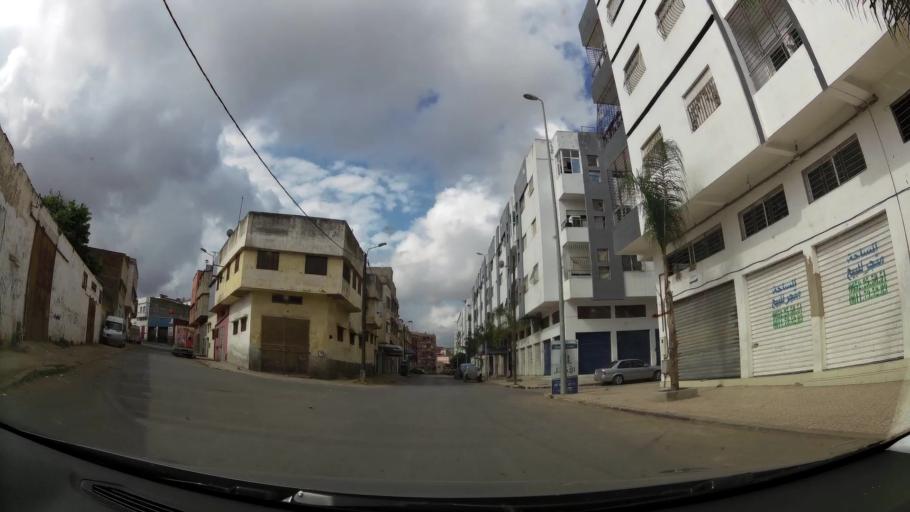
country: MA
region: Gharb-Chrarda-Beni Hssen
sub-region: Kenitra Province
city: Kenitra
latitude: 34.2678
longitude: -6.5655
